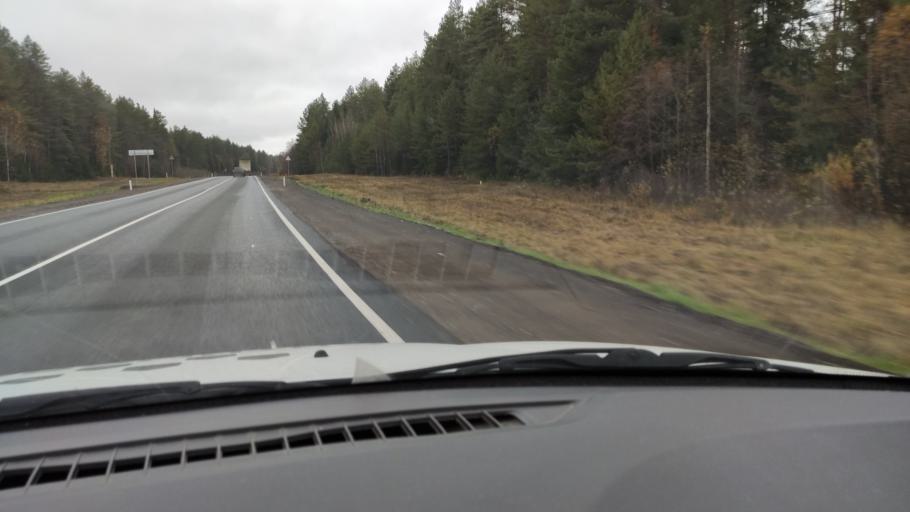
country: RU
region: Kirov
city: Belaya Kholunitsa
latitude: 58.8414
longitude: 50.7762
